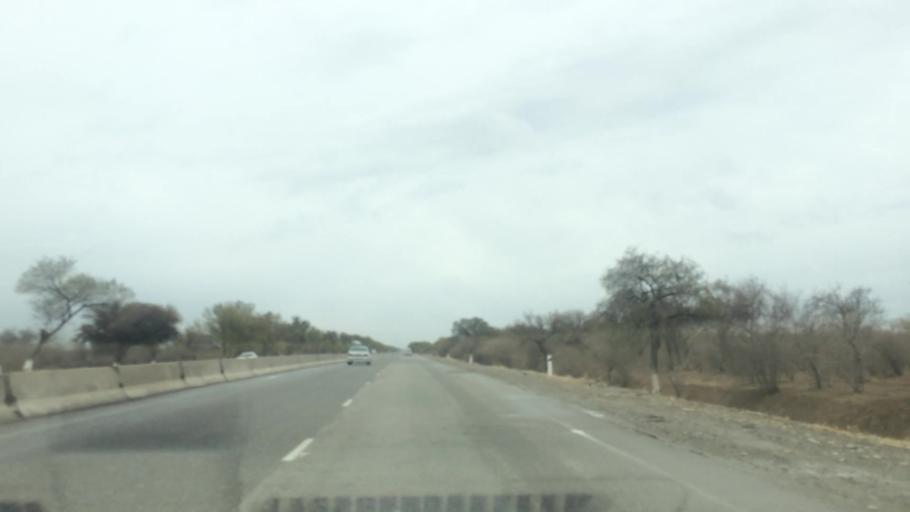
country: UZ
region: Samarqand
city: Bulung'ur
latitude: 39.8173
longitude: 67.3816
